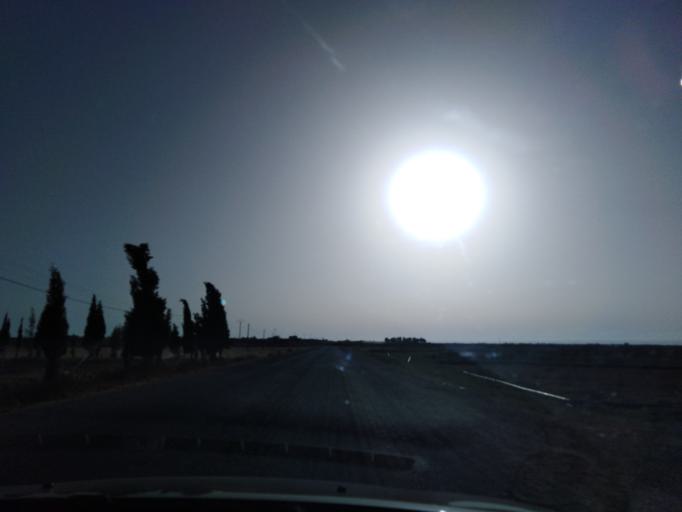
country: MA
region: Doukkala-Abda
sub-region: Safi
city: Safi
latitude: 32.4783
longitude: -8.8867
